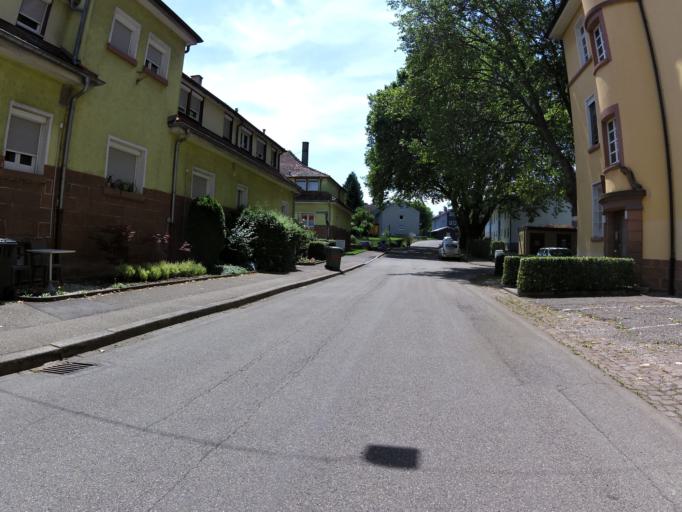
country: DE
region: Baden-Wuerttemberg
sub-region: Freiburg Region
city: Lahr
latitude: 48.3312
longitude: 7.8681
